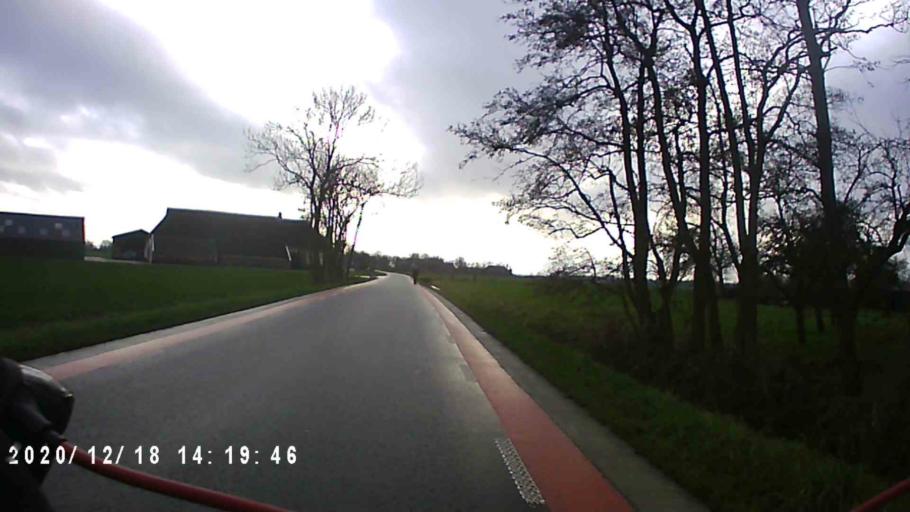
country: NL
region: Groningen
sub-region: Gemeente Bedum
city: Bedum
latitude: 53.2555
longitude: 6.6461
